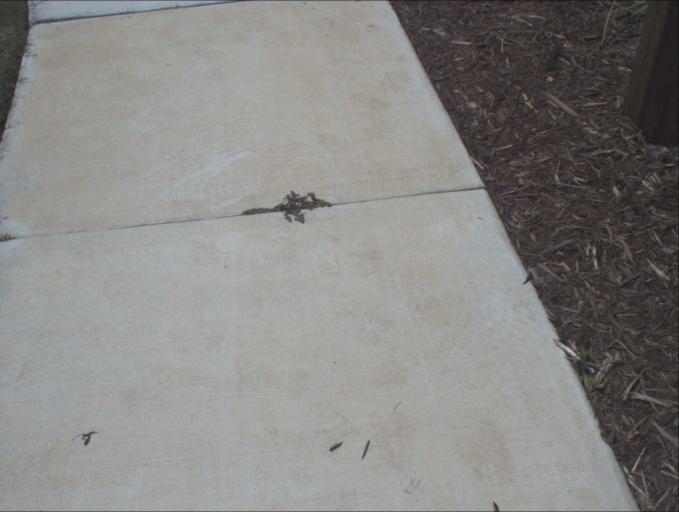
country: AU
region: Queensland
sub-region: Logan
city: Waterford West
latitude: -27.7125
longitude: 153.1422
